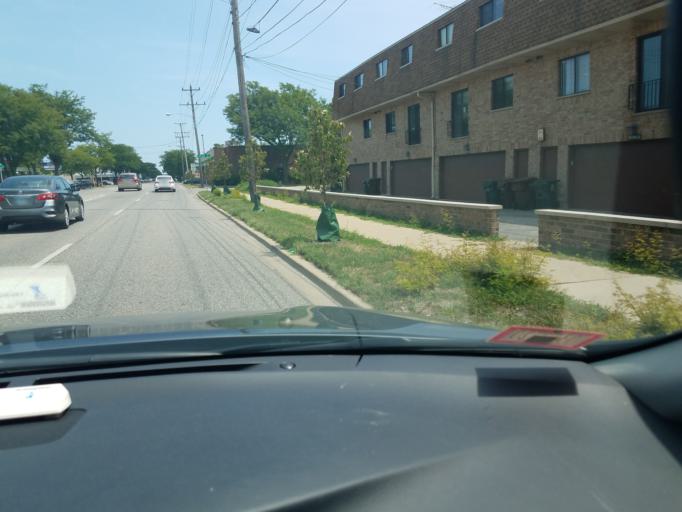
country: US
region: Illinois
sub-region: Cook County
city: Skokie
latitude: 42.0407
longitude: -87.7321
